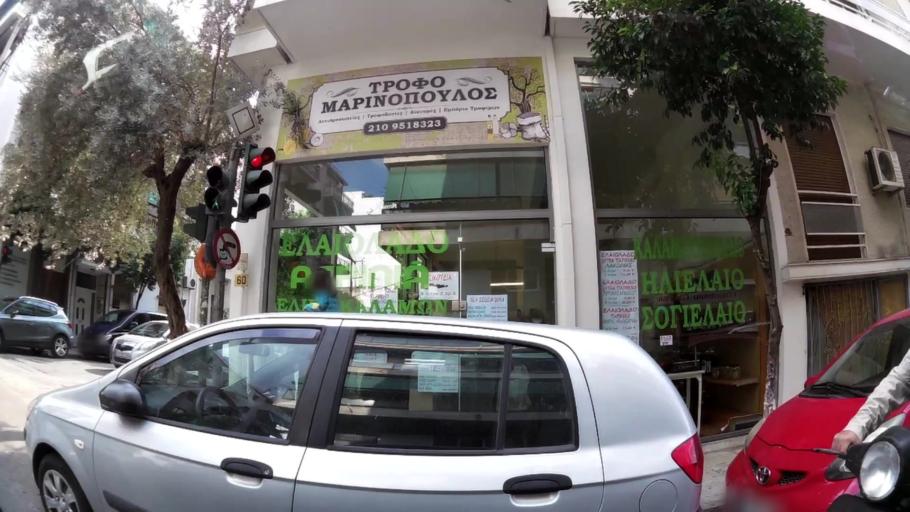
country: GR
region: Attica
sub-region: Nomarchia Athinas
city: Kallithea
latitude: 37.9568
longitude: 23.7096
